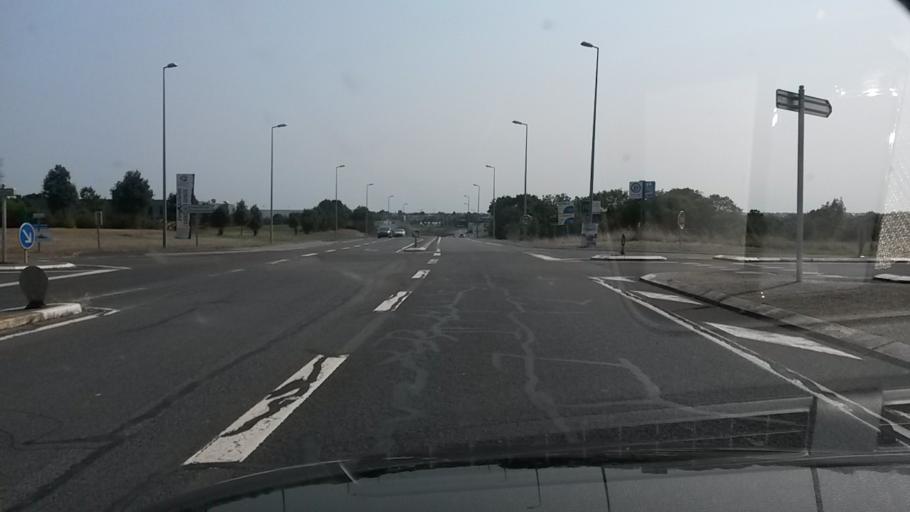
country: FR
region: Pays de la Loire
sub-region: Departement de la Loire-Atlantique
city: Saint-Gereon
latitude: 47.3950
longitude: -1.1896
